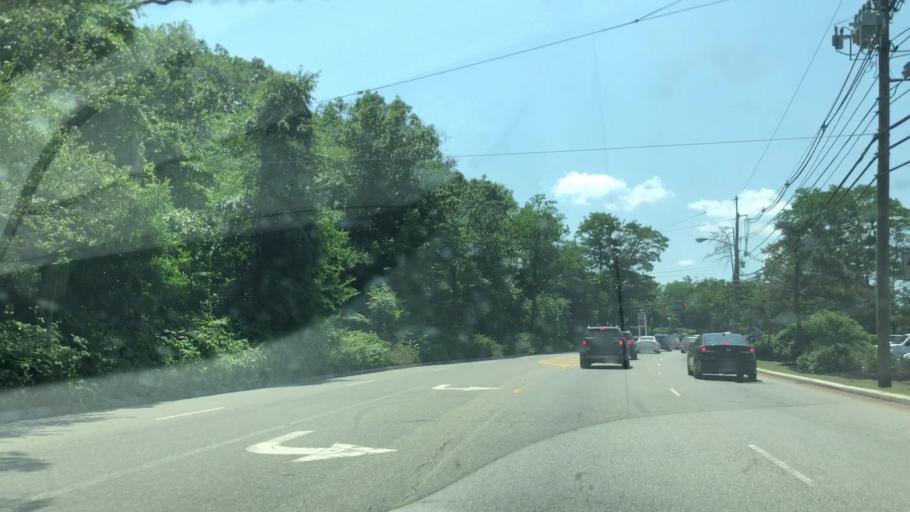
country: US
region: New Jersey
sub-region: Essex County
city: West Orange
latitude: 40.8041
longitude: -74.2471
